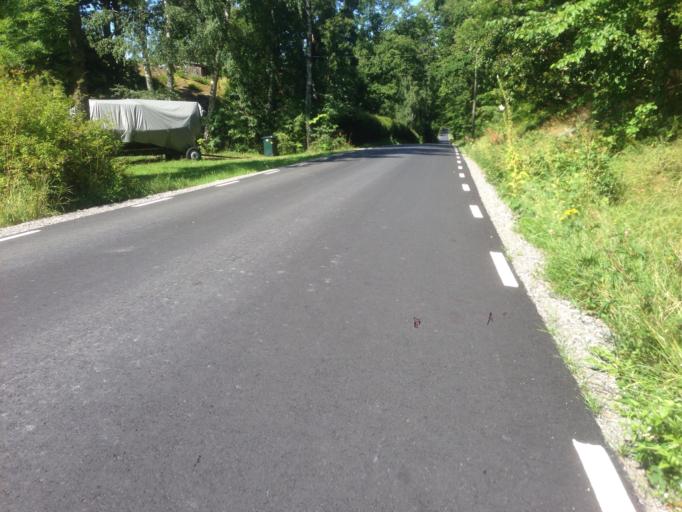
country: SE
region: Stockholm
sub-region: Vaxholms Kommun
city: Vaxholm
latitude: 59.3798
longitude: 18.3766
